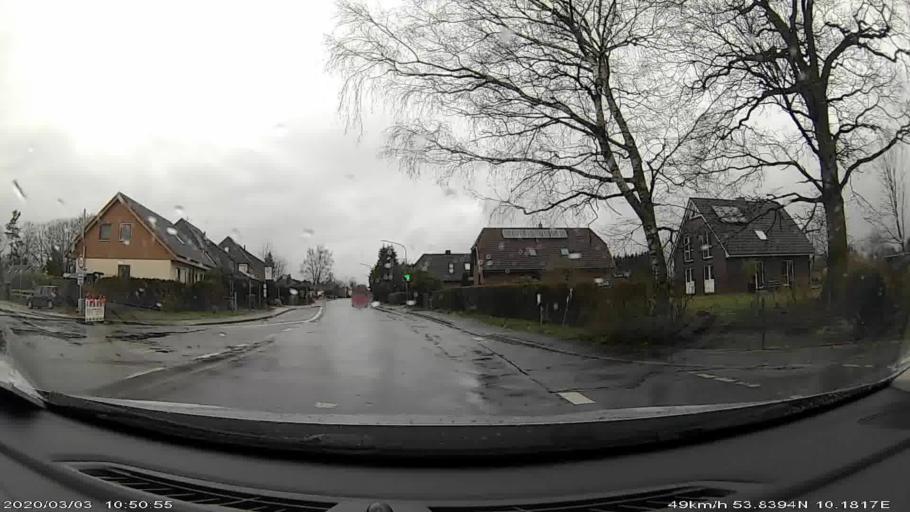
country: DE
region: Schleswig-Holstein
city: Seth
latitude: 53.8413
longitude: 10.1797
